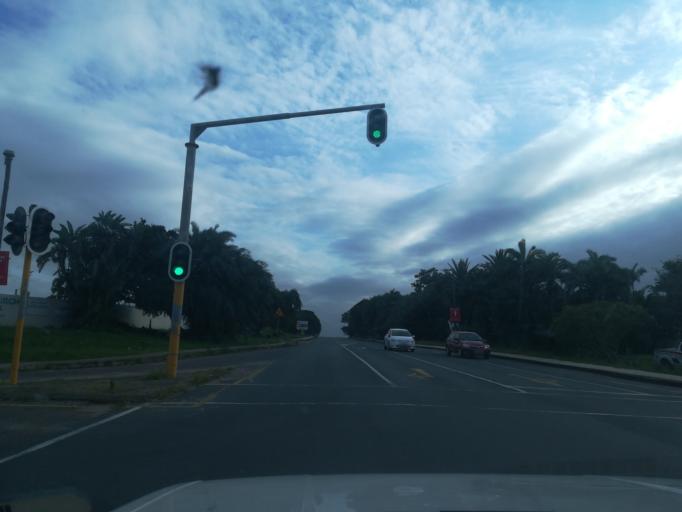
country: ZA
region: KwaZulu-Natal
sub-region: Ugu District Municipality
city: Scottburgh
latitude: -30.2946
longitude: 30.7412
